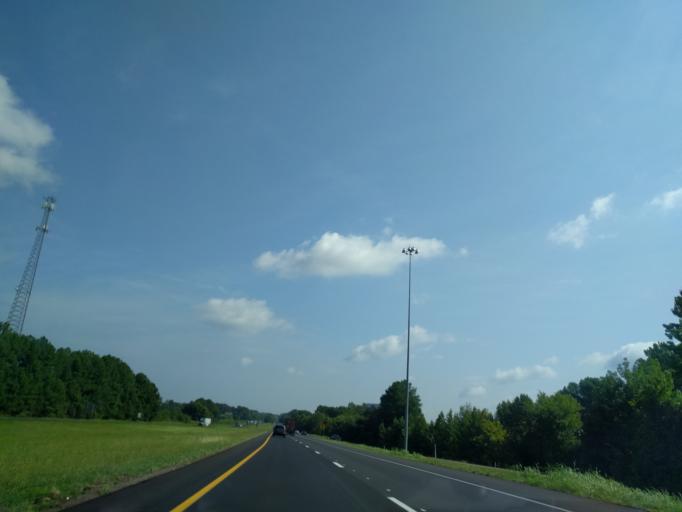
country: US
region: Tennessee
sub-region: Sumner County
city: White House
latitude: 36.4704
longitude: -86.6816
